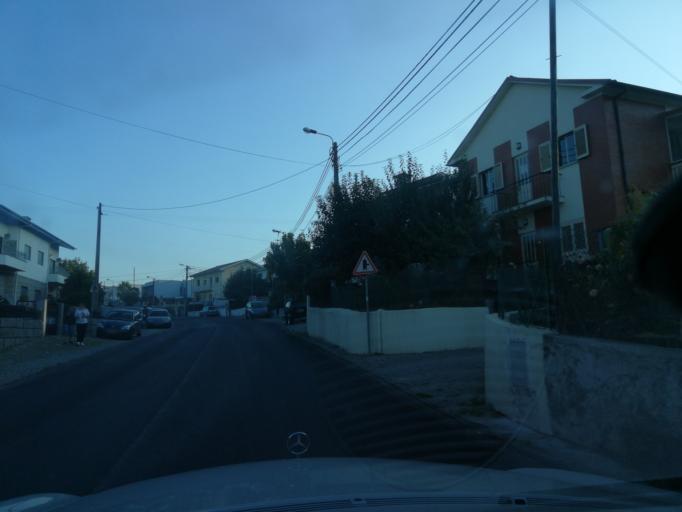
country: PT
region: Braga
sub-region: Braga
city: Braga
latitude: 41.5260
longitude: -8.4285
